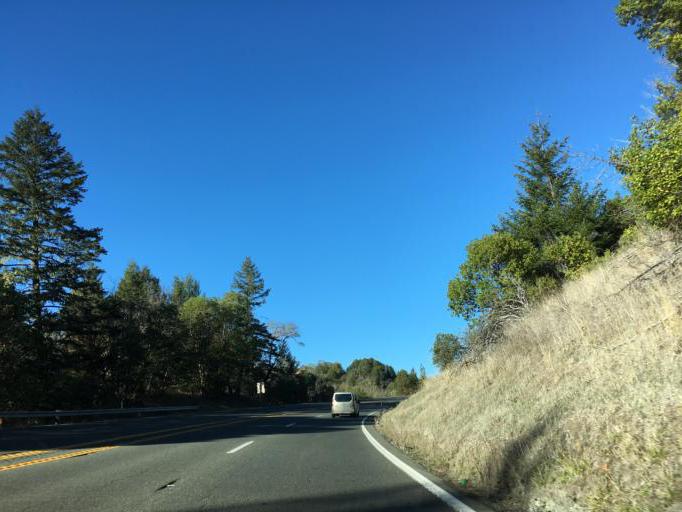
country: US
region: California
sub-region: Mendocino County
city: Laytonville
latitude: 39.6194
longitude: -123.4648
